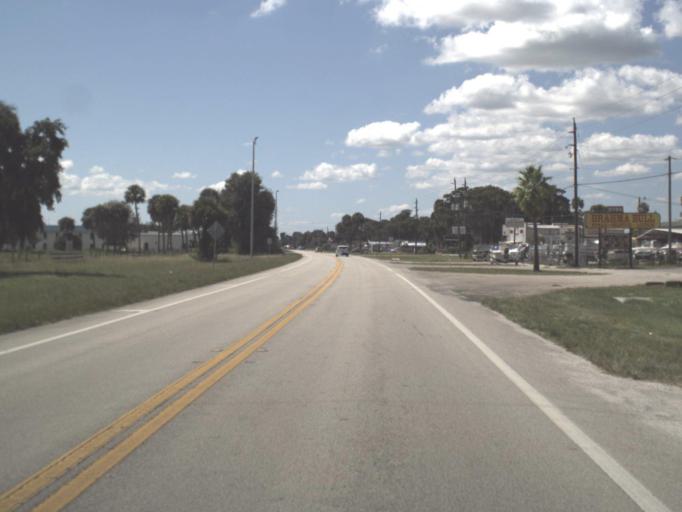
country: US
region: Florida
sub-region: Okeechobee County
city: Taylor Creek
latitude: 27.2094
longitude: -80.8025
